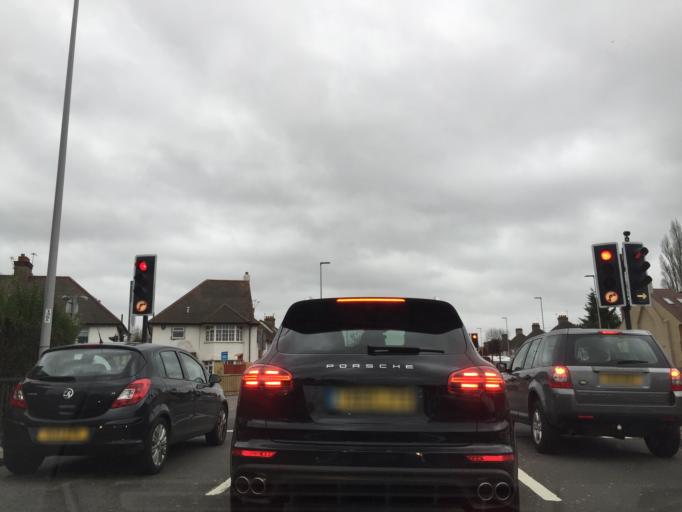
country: GB
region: England
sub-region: Greater London
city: Hendon
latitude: 51.5671
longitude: -0.2066
